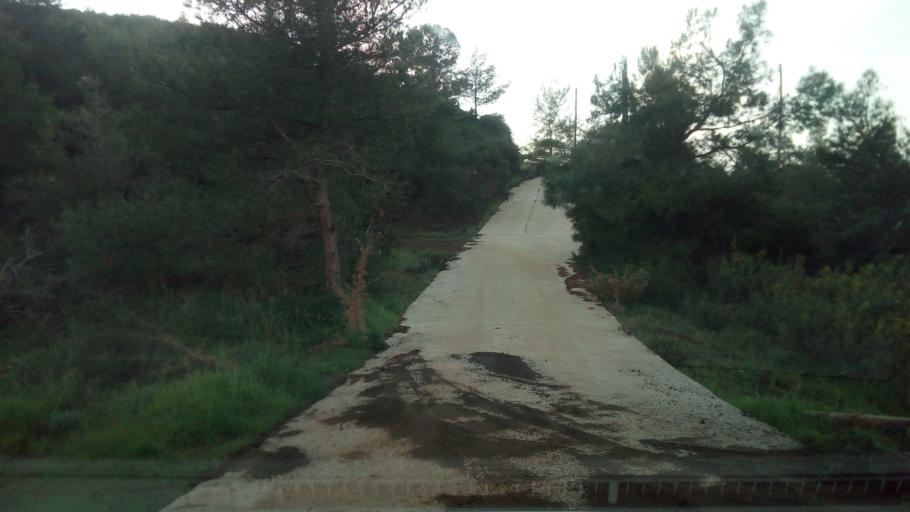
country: CY
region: Lefkosia
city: Kato Pyrgos
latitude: 35.1717
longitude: 32.6686
